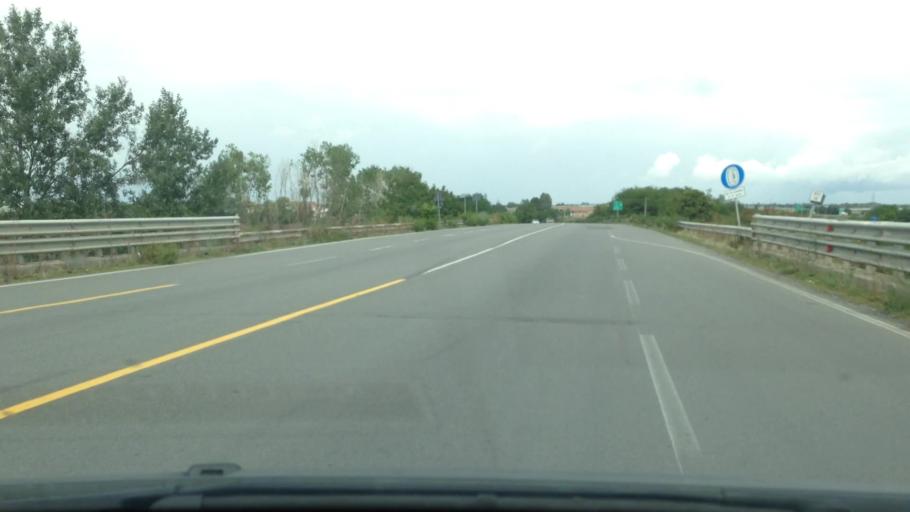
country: IT
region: Piedmont
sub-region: Provincia di Alessandria
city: Tortona
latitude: 44.8958
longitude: 8.8398
